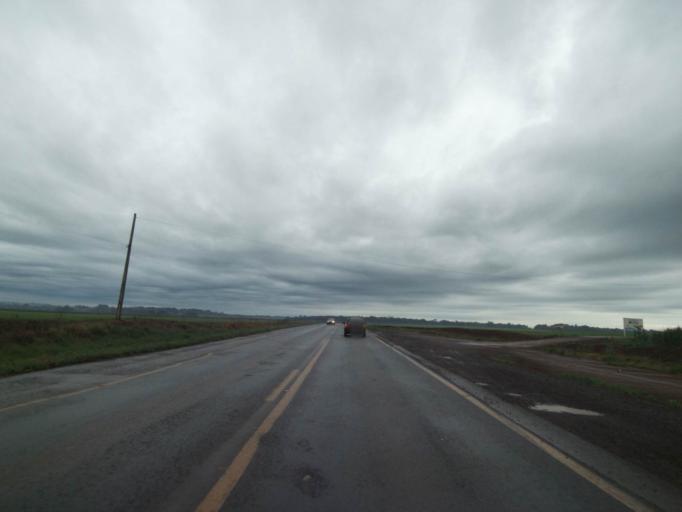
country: BR
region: Parana
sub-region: Toledo
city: Toledo
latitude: -24.6936
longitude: -53.7432
